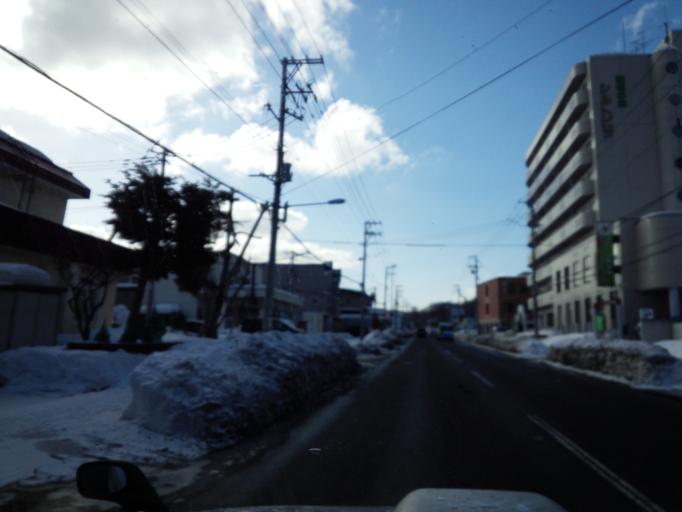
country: JP
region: Hokkaido
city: Sapporo
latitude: 42.9563
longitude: 141.3440
